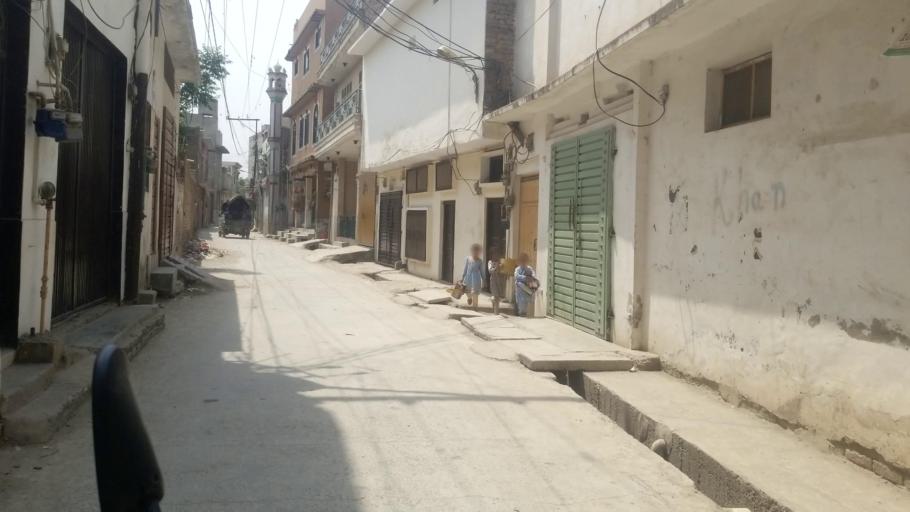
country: PK
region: Khyber Pakhtunkhwa
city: Peshawar
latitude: 34.0261
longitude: 71.5809
